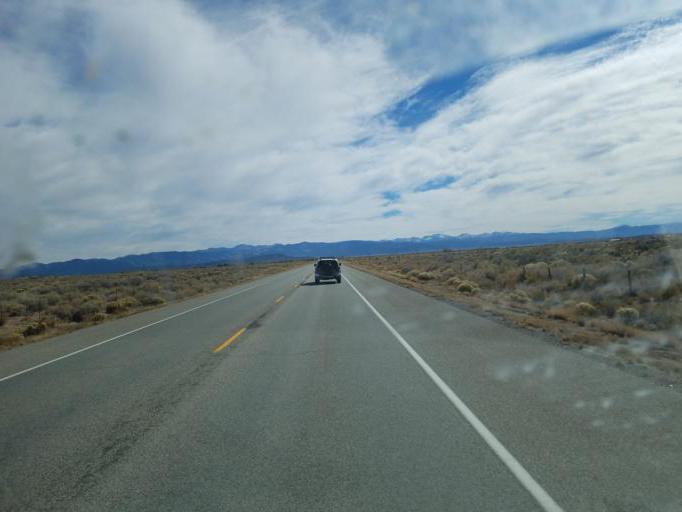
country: US
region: Colorado
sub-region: Costilla County
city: San Luis
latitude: 37.4478
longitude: -105.5388
